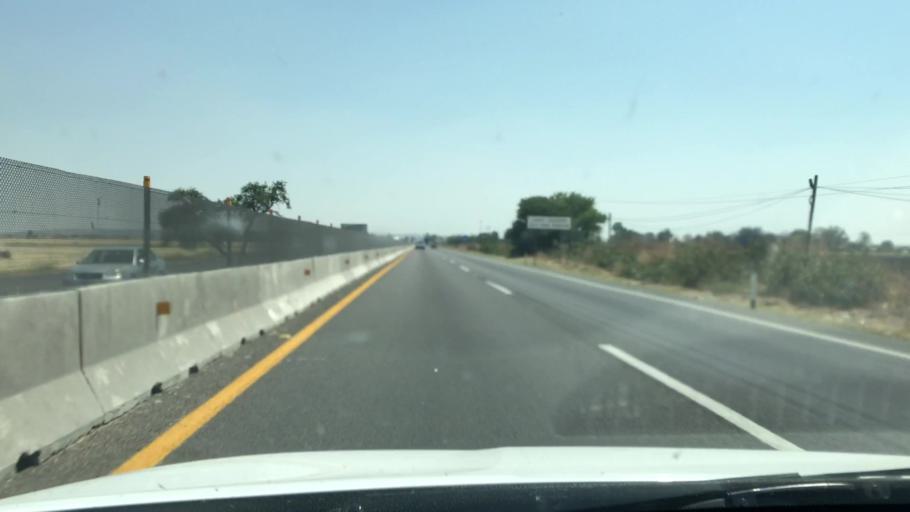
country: MX
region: Guanajuato
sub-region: Abasolo
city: San Bernardo Pena Blanca
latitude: 20.4795
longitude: -101.4968
